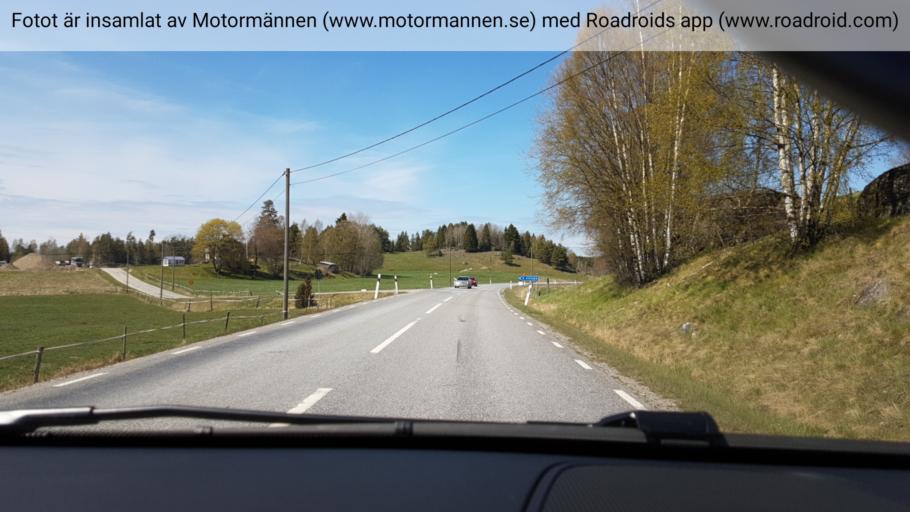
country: SE
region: Stockholm
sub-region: Nynashamns Kommun
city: Osmo
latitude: 59.0199
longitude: 17.7998
